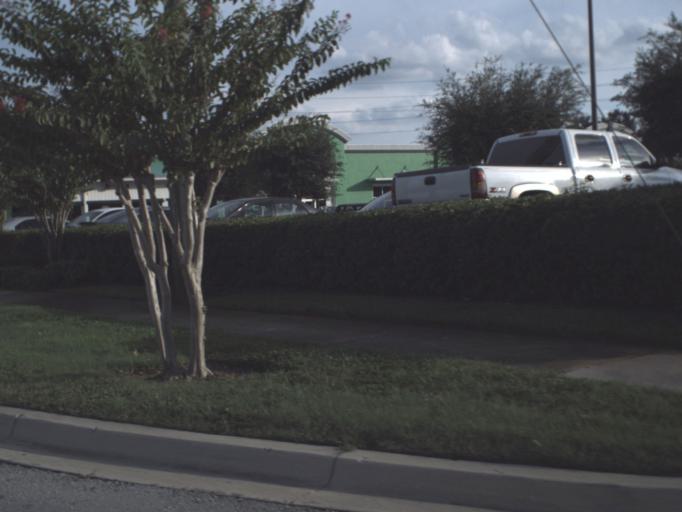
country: US
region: Florida
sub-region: Polk County
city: Combee Settlement
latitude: 28.0502
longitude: -81.9271
